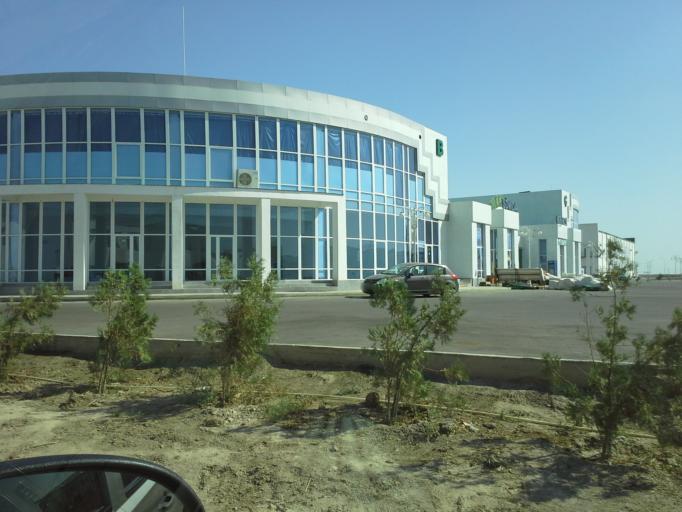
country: TM
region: Dasoguz
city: Dasoguz
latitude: 41.8093
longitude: 59.9547
